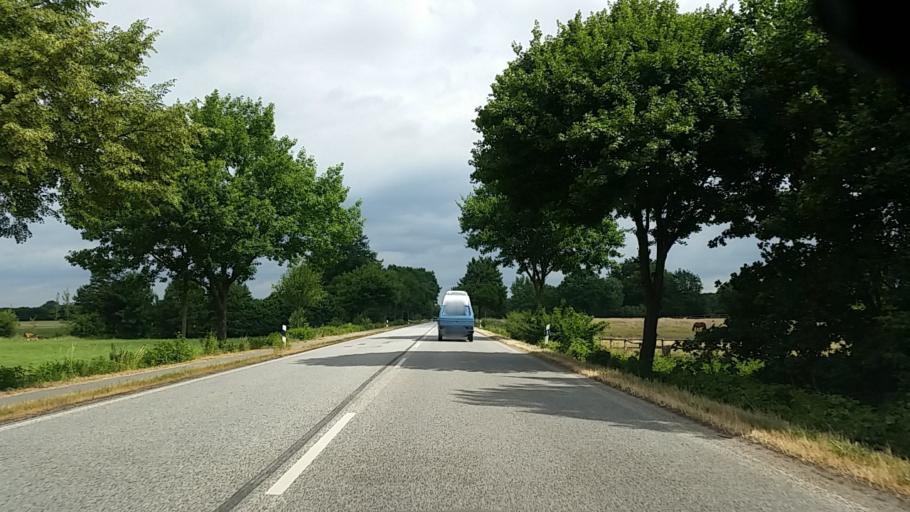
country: DE
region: Schleswig-Holstein
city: Elmenhorst
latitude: 53.7708
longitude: 10.2684
